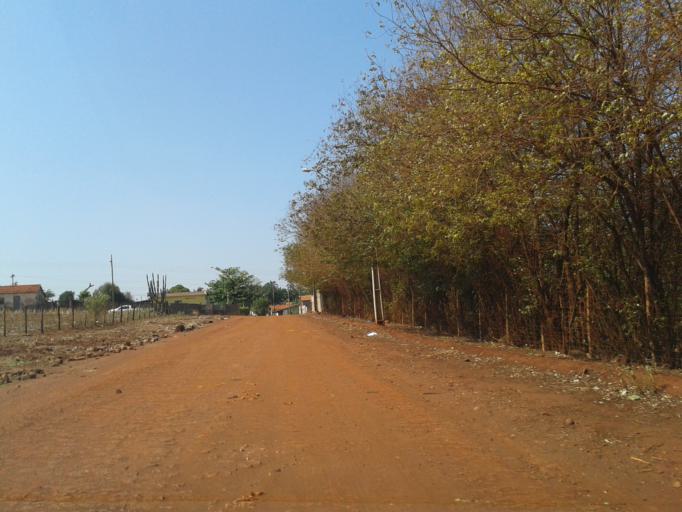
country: BR
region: Minas Gerais
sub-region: Ituiutaba
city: Ituiutaba
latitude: -18.9545
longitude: -49.4531
